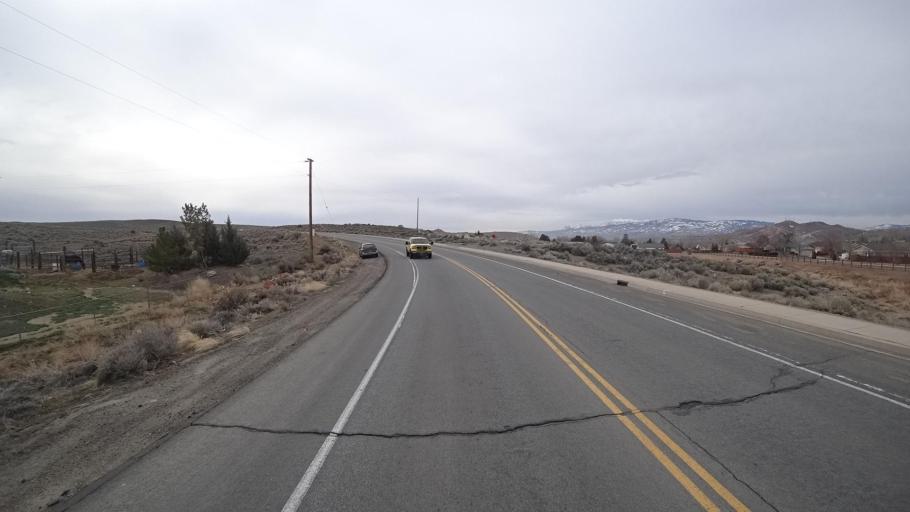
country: US
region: Nevada
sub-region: Washoe County
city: Sun Valley
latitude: 39.6110
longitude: -119.7616
